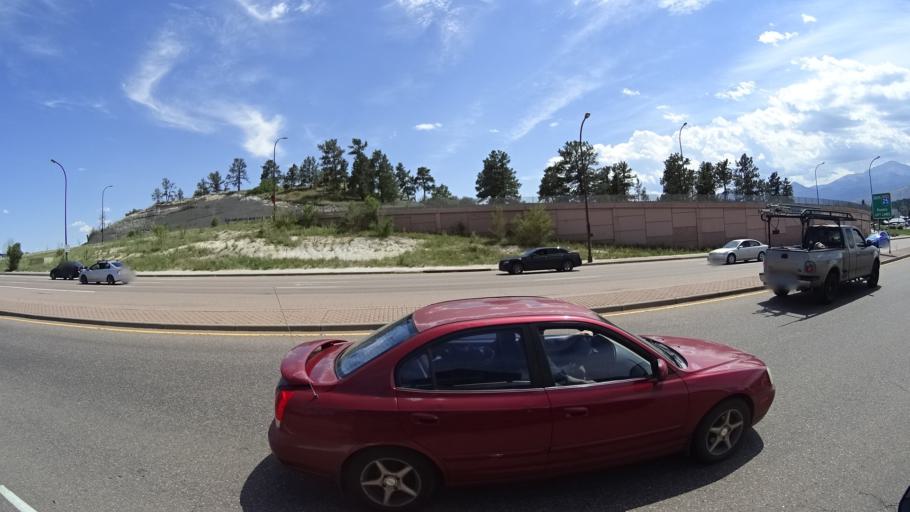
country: US
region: Colorado
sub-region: El Paso County
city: Air Force Academy
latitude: 38.9331
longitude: -104.8095
